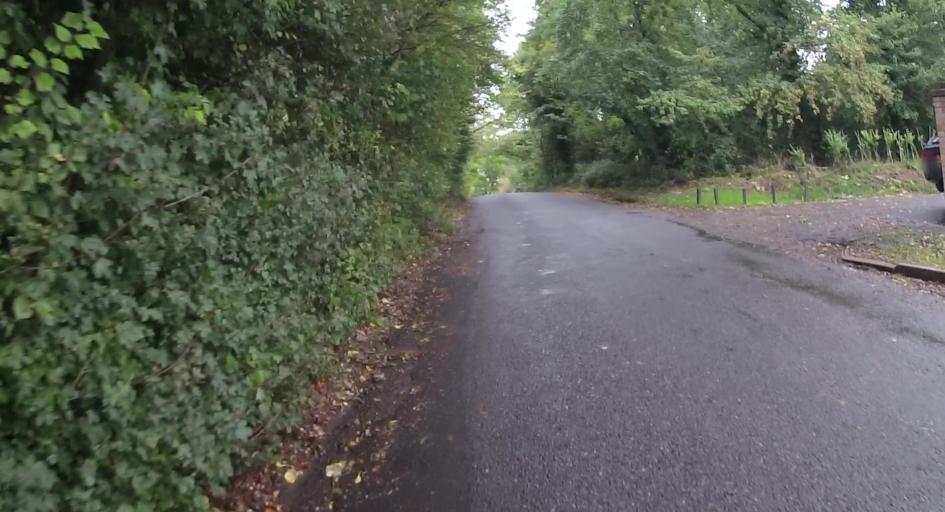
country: GB
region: England
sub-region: West Berkshire
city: Thatcham
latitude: 51.4216
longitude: -1.1796
